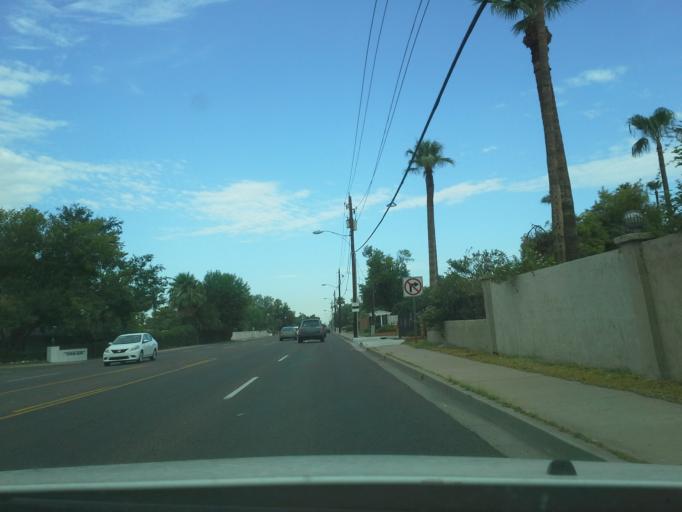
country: US
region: Arizona
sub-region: Maricopa County
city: Phoenix
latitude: 33.5239
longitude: -112.0754
